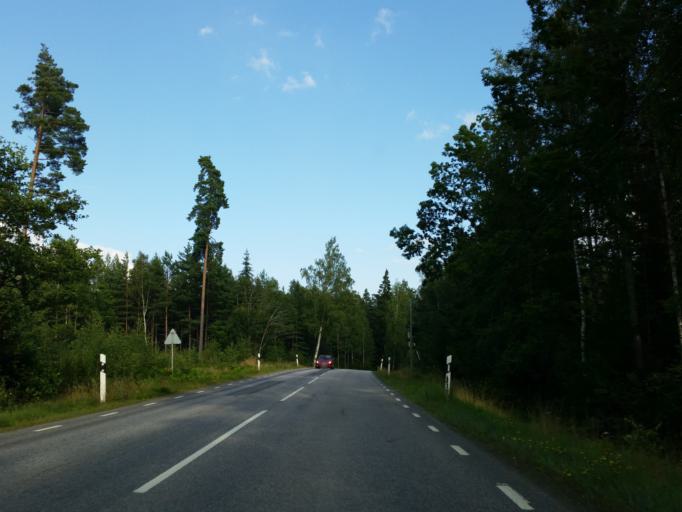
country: SE
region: Stockholm
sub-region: Nykvarns Kommun
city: Nykvarn
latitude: 59.2069
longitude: 17.3835
